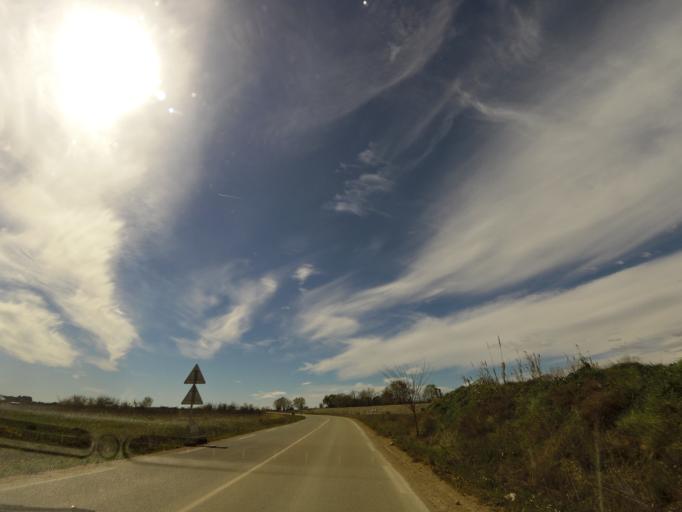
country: FR
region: Languedoc-Roussillon
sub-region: Departement du Gard
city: Gallargues-le-Montueux
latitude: 43.7003
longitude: 4.1677
